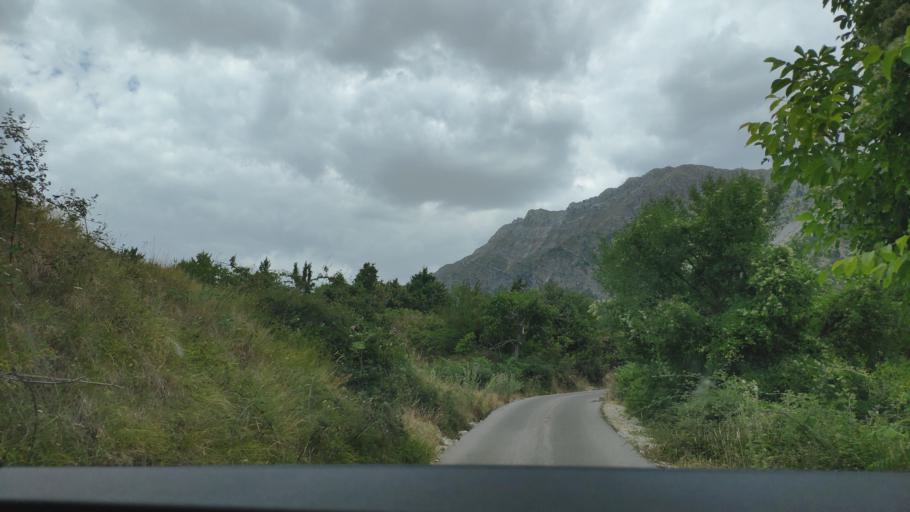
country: GR
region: Epirus
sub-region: Nomos Artas
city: Voulgareli
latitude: 39.4384
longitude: 21.2046
